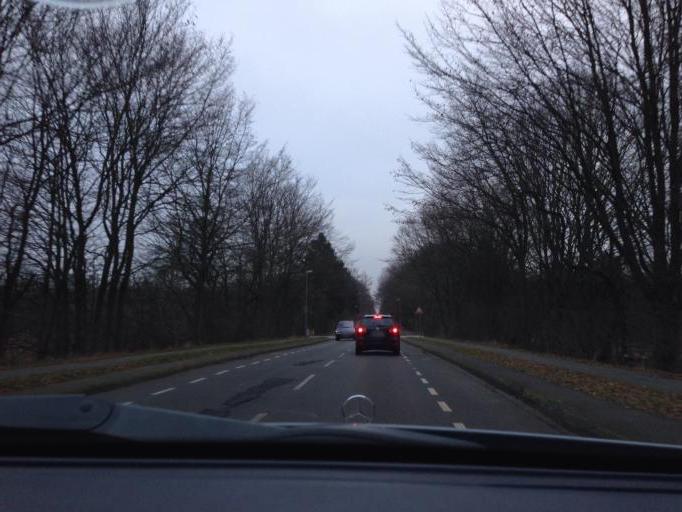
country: DE
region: Schleswig-Holstein
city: Ahrensburg
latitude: 53.6591
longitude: 10.2360
